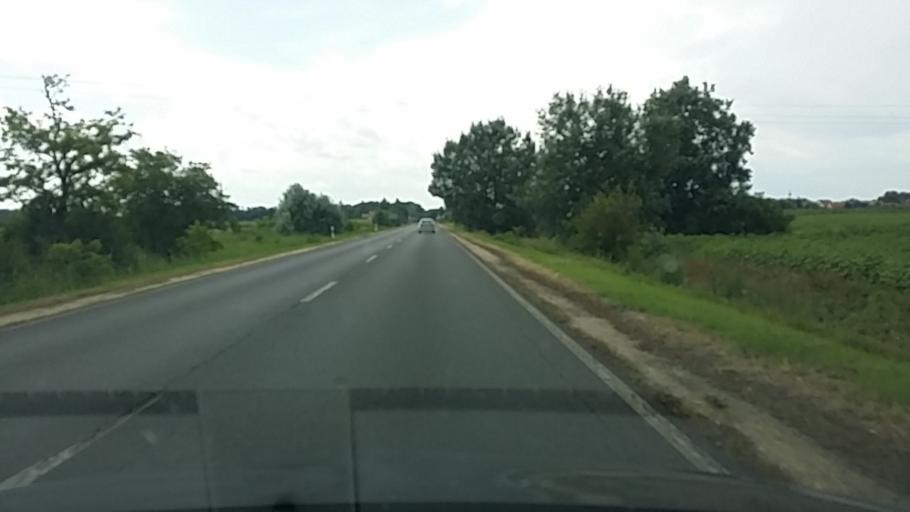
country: HU
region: Pest
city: Orkeny
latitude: 47.1189
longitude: 19.4426
